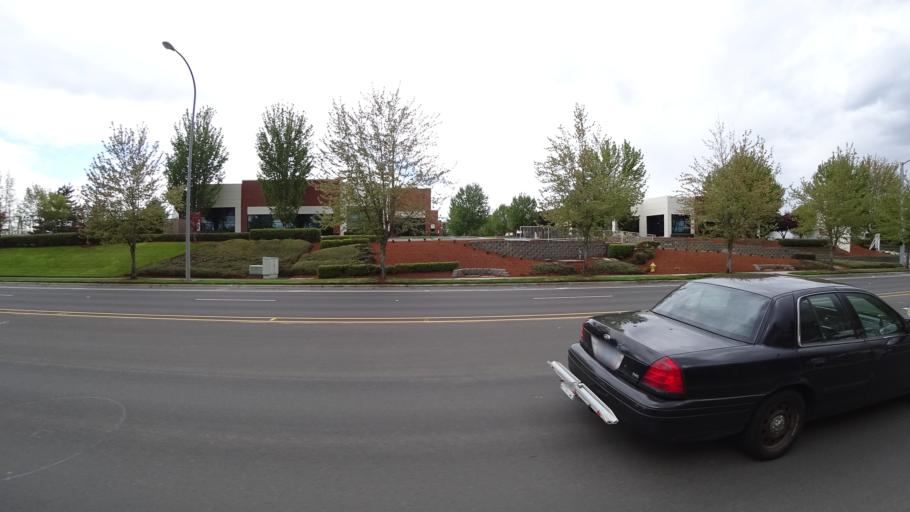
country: US
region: Oregon
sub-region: Washington County
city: Rockcreek
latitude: 45.5508
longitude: -122.9152
